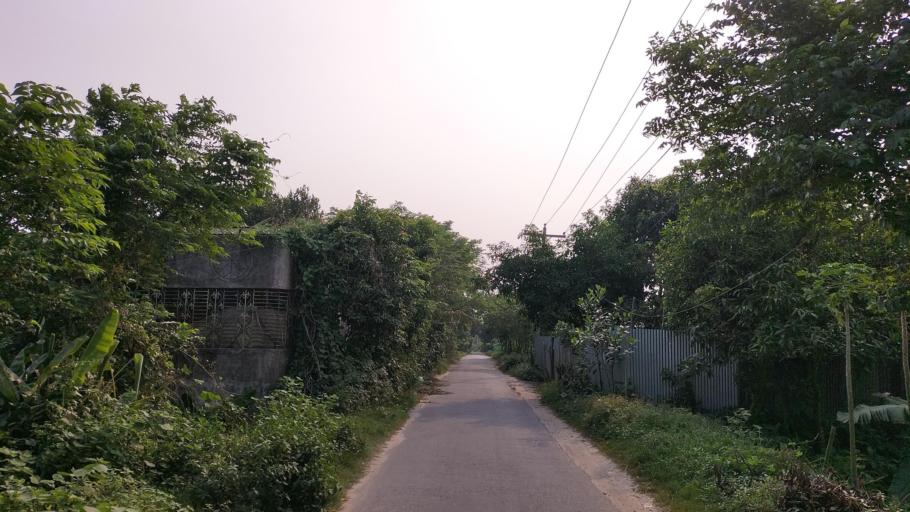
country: BD
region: Dhaka
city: Azimpur
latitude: 23.6739
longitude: 90.3139
